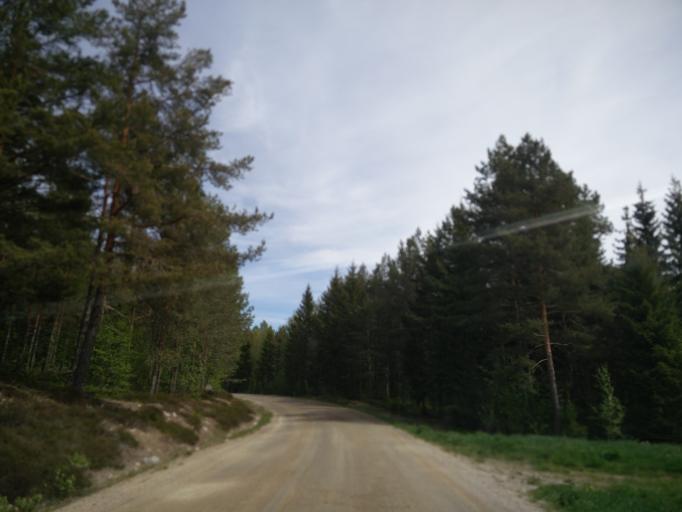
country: SE
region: Gaevleborg
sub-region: Hudiksvalls Kommun
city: Sorforsa
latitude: 61.7388
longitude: 16.9601
